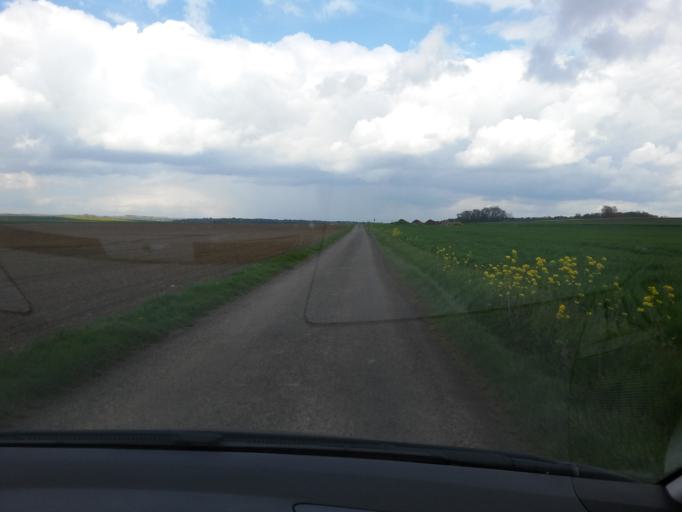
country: FR
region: Picardie
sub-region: Departement de l'Oise
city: Chevrieres
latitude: 49.3563
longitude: 2.6833
